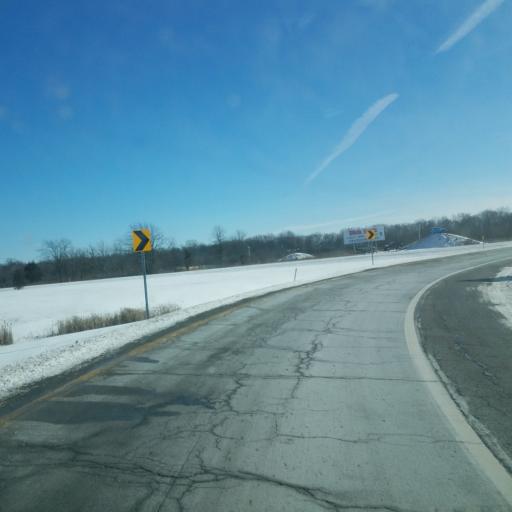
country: US
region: Michigan
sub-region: Livingston County
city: Fowlerville
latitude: 42.6463
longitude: -84.0716
